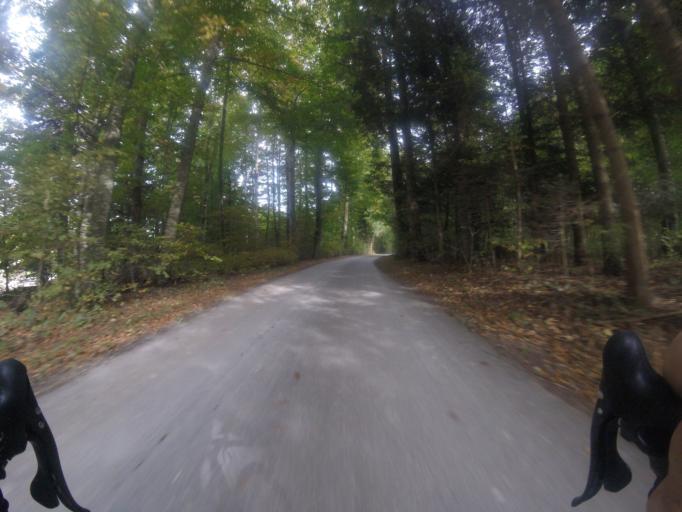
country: CH
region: Bern
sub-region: Bern-Mittelland District
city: Muhleberg
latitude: 46.9309
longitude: 7.2883
